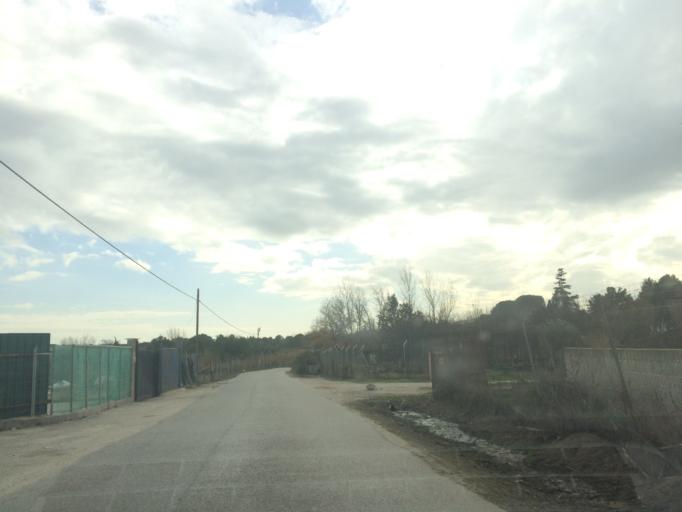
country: ES
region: Madrid
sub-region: Provincia de Madrid
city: Arroyomolinos
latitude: 40.3060
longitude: -3.9460
